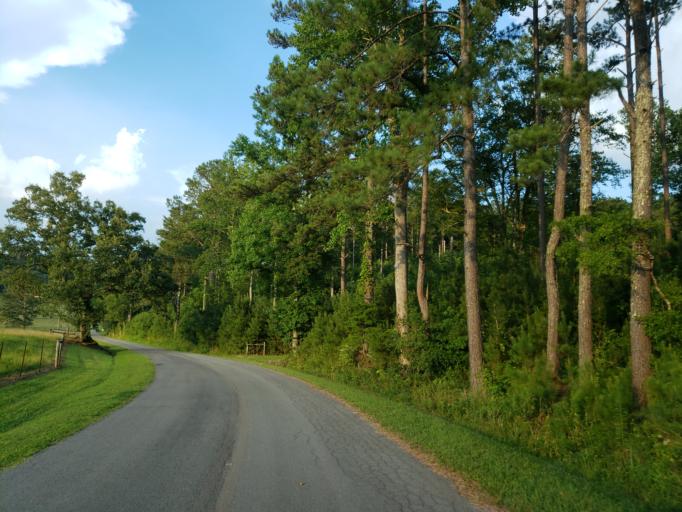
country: US
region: Georgia
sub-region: Polk County
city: Aragon
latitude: 34.0556
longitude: -84.9847
